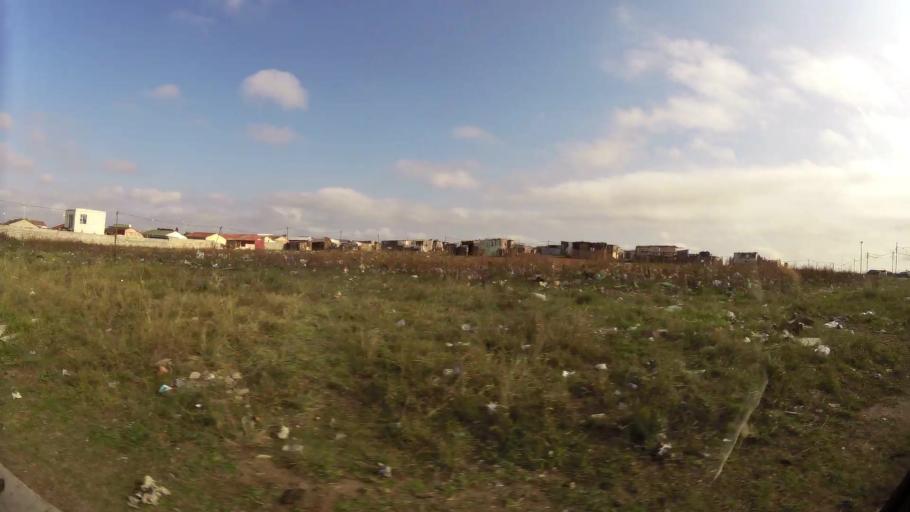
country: ZA
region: Eastern Cape
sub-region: Nelson Mandela Bay Metropolitan Municipality
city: Port Elizabeth
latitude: -33.9174
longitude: 25.5384
